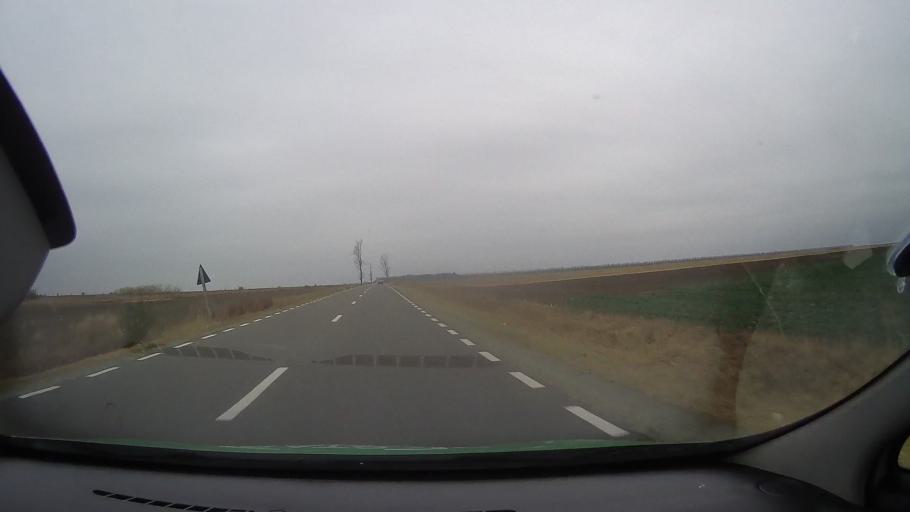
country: RO
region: Ialomita
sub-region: Comuna Scanteia
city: Iazu
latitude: 44.7130
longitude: 27.4192
